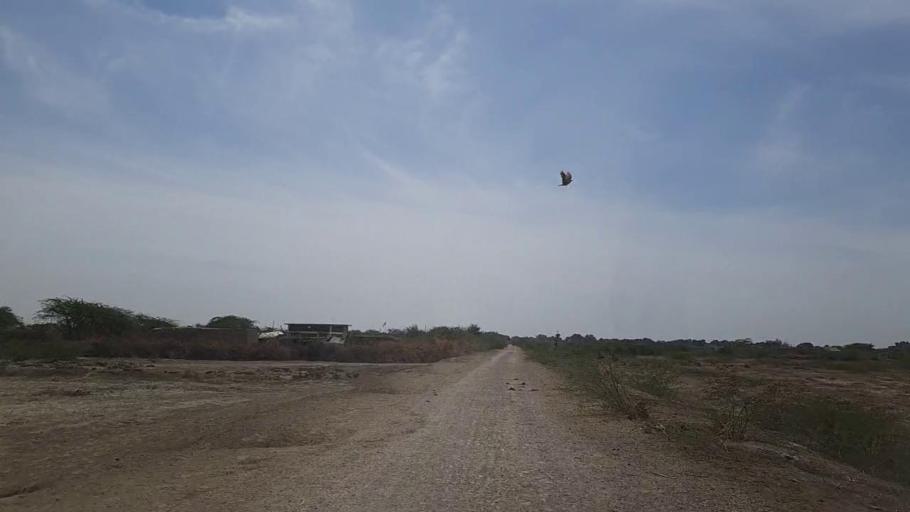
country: PK
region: Sindh
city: Samaro
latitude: 25.2695
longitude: 69.4785
